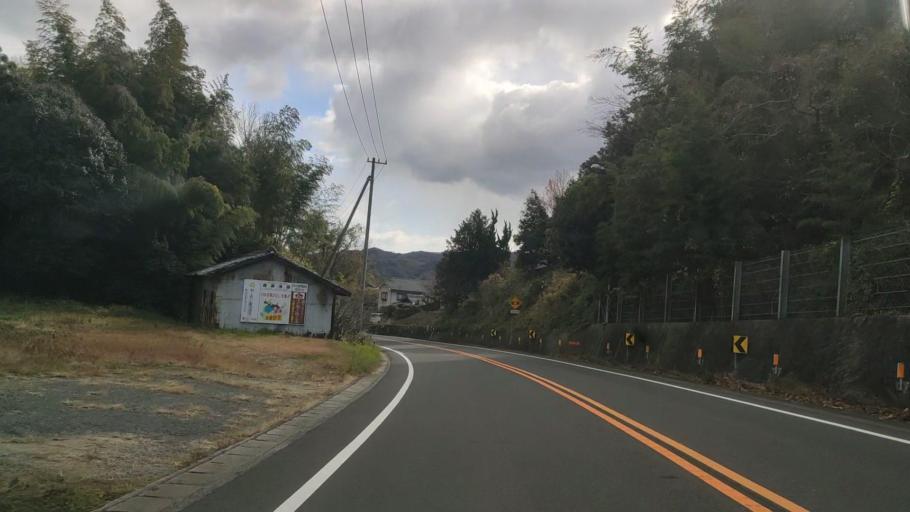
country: JP
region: Ehime
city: Hojo
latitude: 34.0606
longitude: 132.9159
